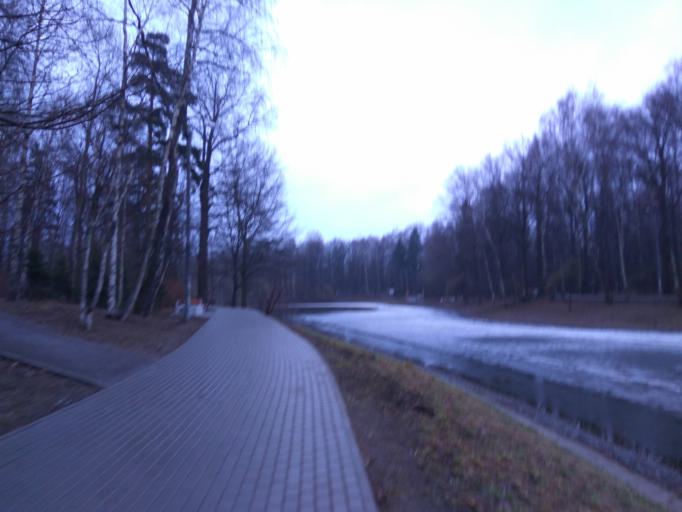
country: RU
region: Moscow
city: Vagonoremont
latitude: 55.9011
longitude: 37.5622
